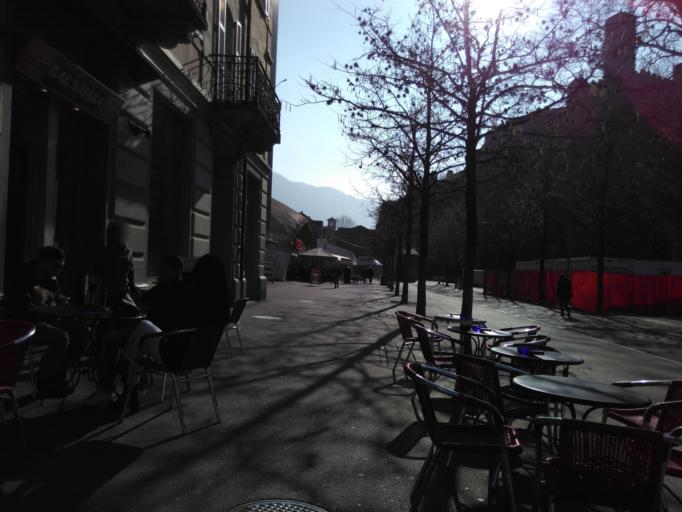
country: CH
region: Ticino
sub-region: Bellinzona District
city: Bellinzona
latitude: 46.1943
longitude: 9.0242
